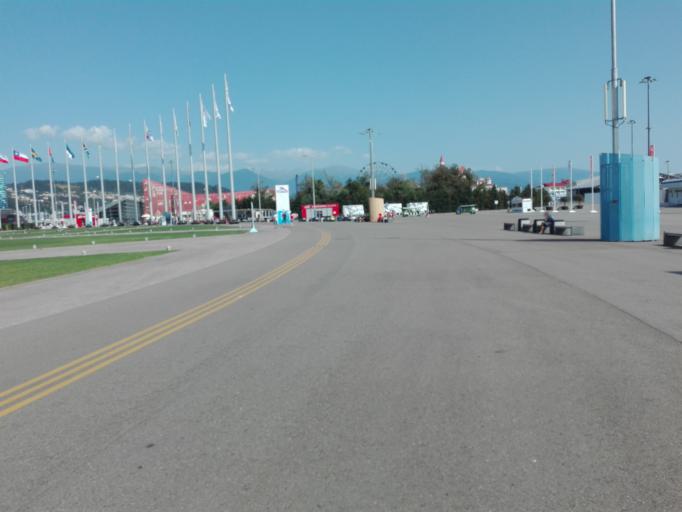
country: RU
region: Krasnodarskiy
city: Adler
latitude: 43.4046
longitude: 39.9543
